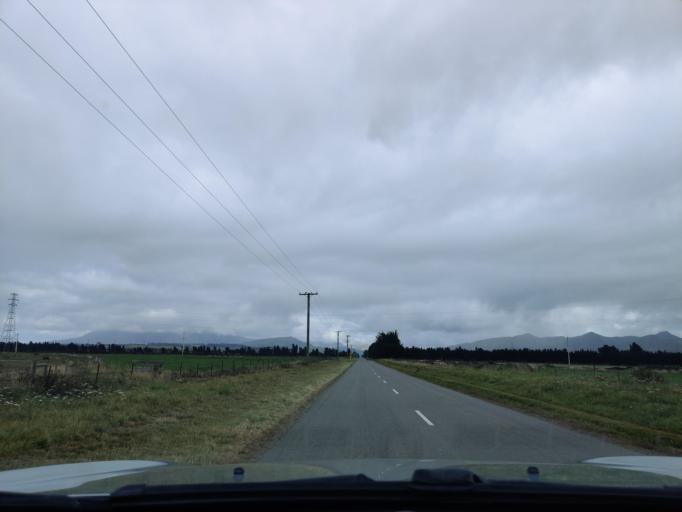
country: NZ
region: Canterbury
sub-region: Hurunui District
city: Amberley
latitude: -43.0773
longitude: 172.7231
